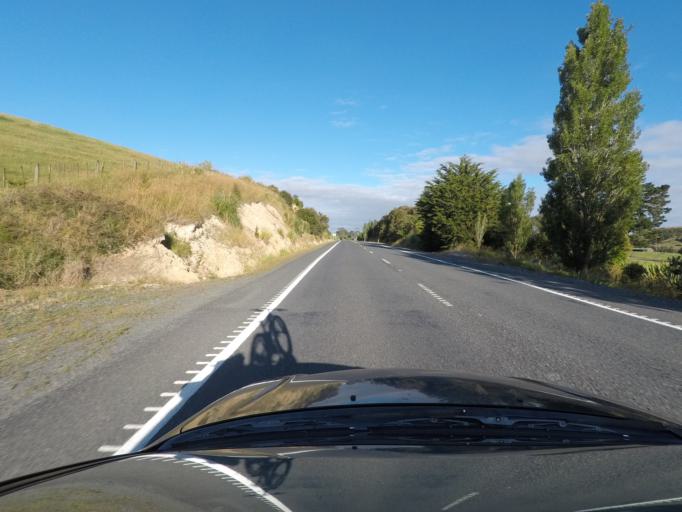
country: NZ
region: Northland
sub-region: Far North District
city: Kawakawa
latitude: -35.5181
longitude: 174.1931
